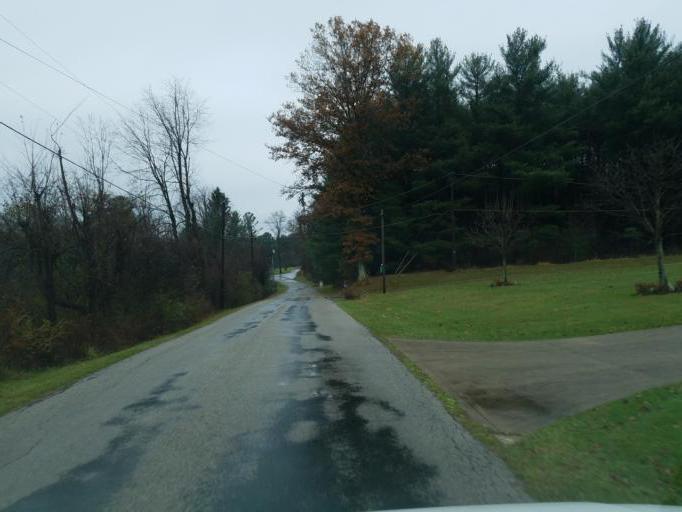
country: US
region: Ohio
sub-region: Richland County
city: Ontario
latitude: 40.7288
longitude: -82.6036
